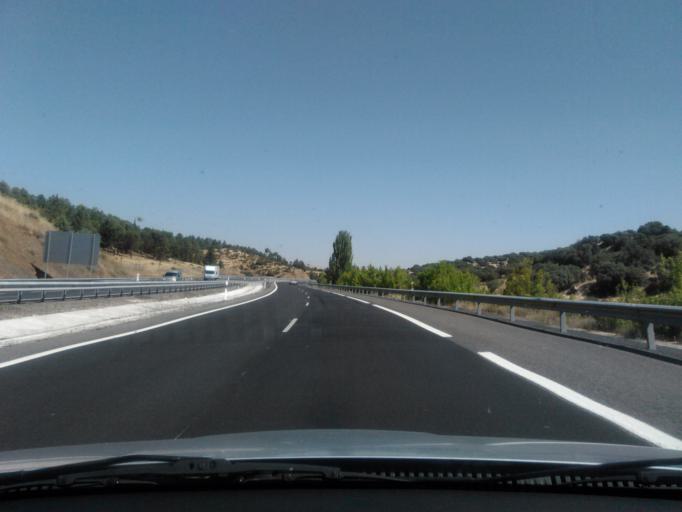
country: ES
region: Castille-La Mancha
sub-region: Provincia de Ciudad Real
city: Viso del Marques
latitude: 38.4425
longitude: -3.4962
